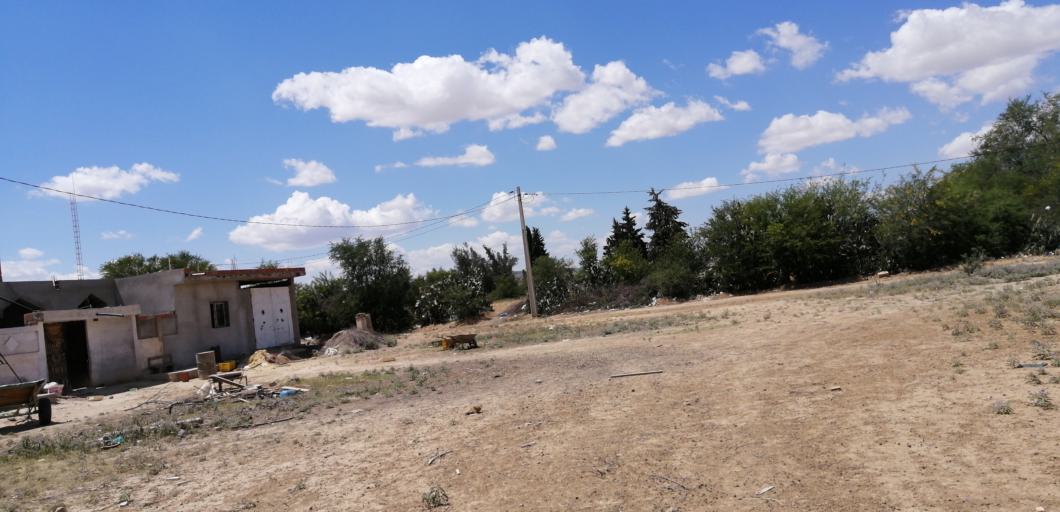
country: TN
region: Al Qayrawan
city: Kairouan
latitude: 35.6170
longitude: 9.9226
